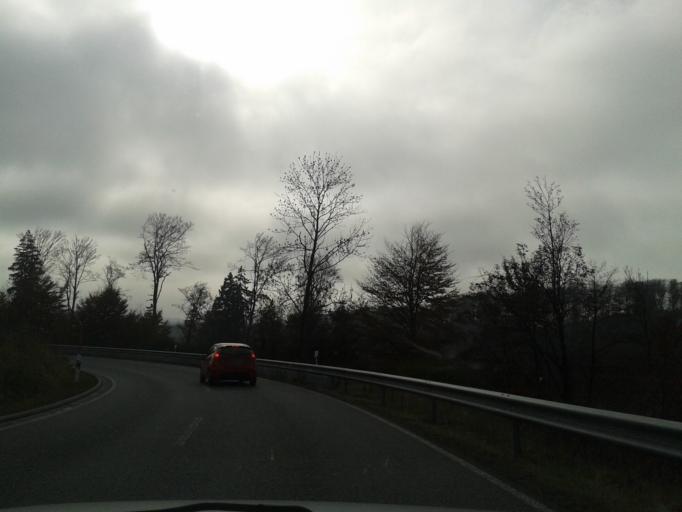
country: DE
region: North Rhine-Westphalia
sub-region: Regierungsbezirk Arnsberg
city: Bad Berleburg
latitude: 51.1349
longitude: 8.4230
